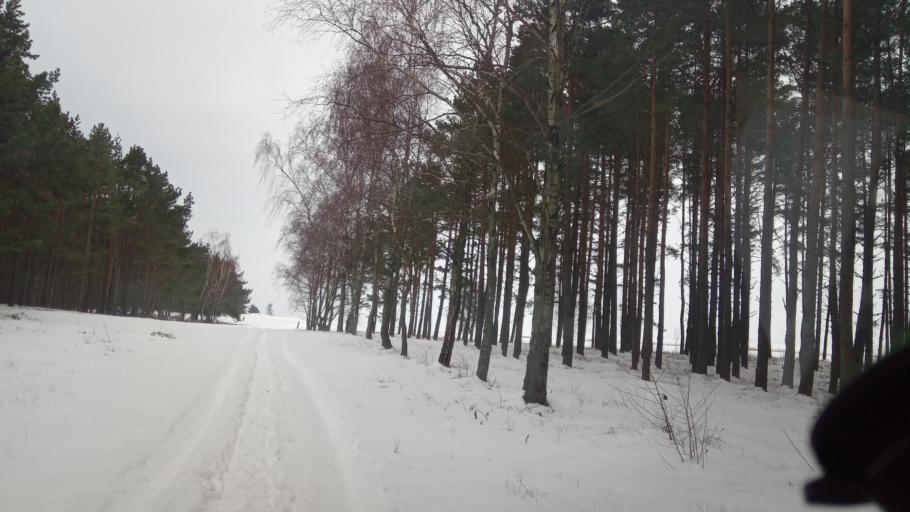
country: LT
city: Neringa
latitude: 55.4215
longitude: 21.1077
